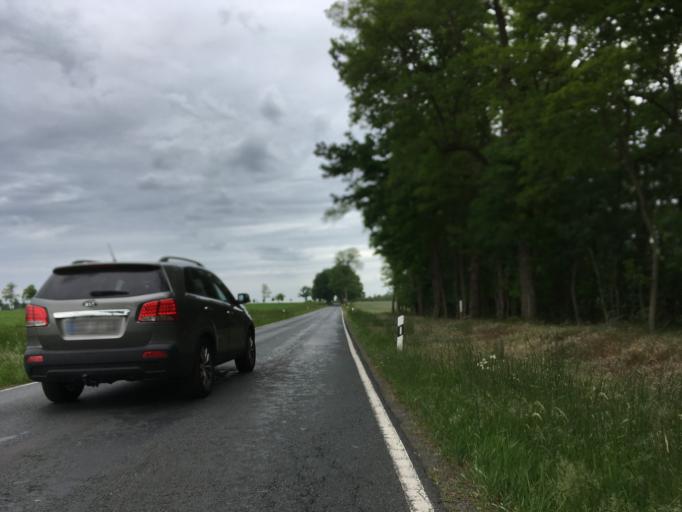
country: DE
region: Brandenburg
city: Bernau bei Berlin
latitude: 52.6687
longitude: 13.6373
